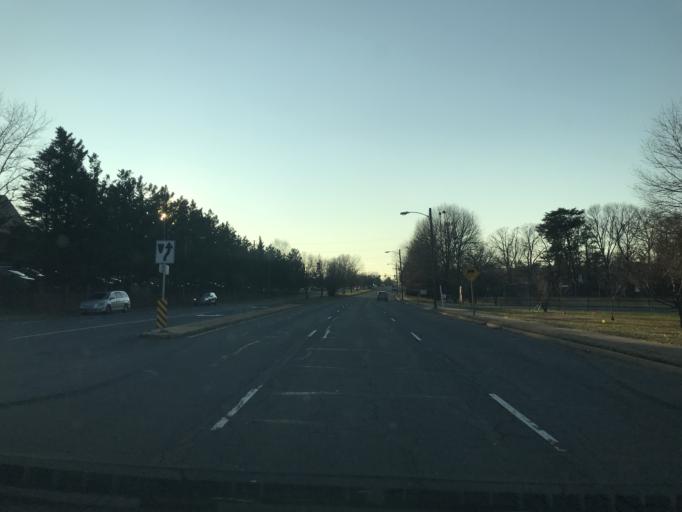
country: US
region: Virginia
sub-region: Fairfax County
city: Franconia
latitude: 38.7810
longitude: -77.1523
